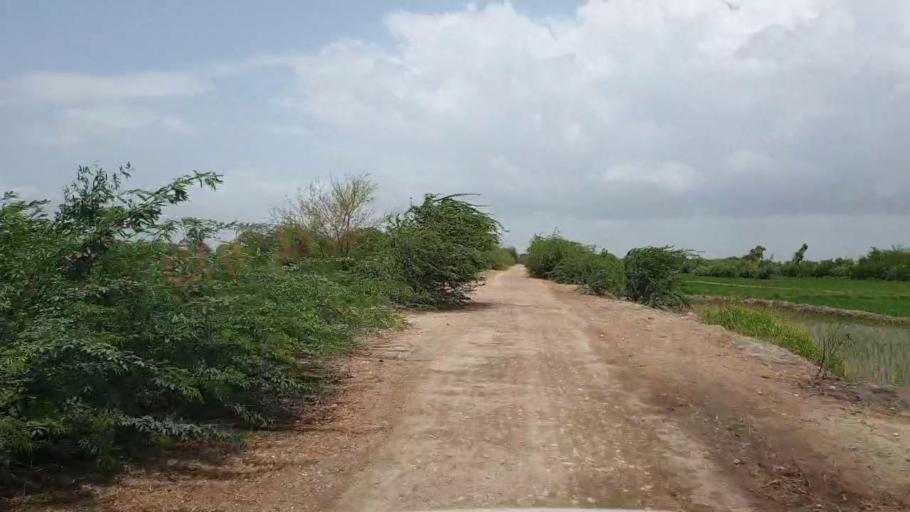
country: PK
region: Sindh
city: Kario
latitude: 24.6947
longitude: 68.6472
